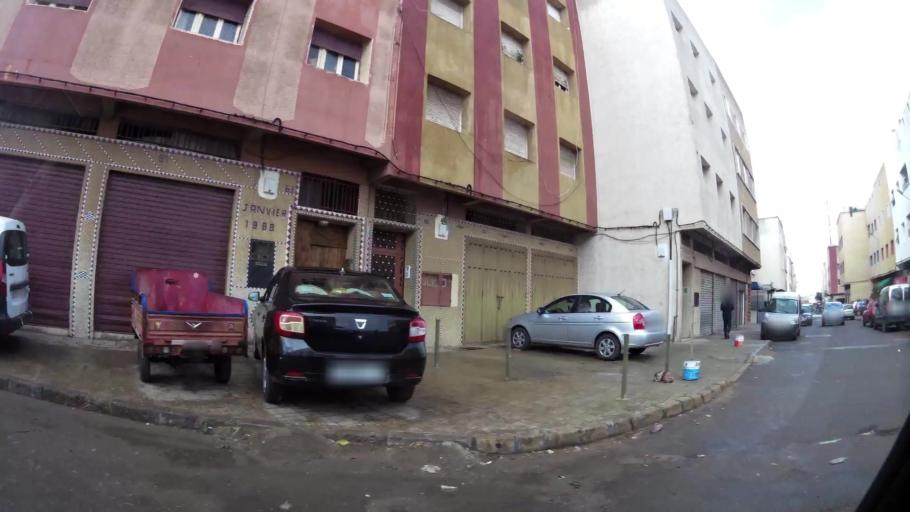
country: MA
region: Grand Casablanca
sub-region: Casablanca
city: Casablanca
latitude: 33.5600
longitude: -7.6841
